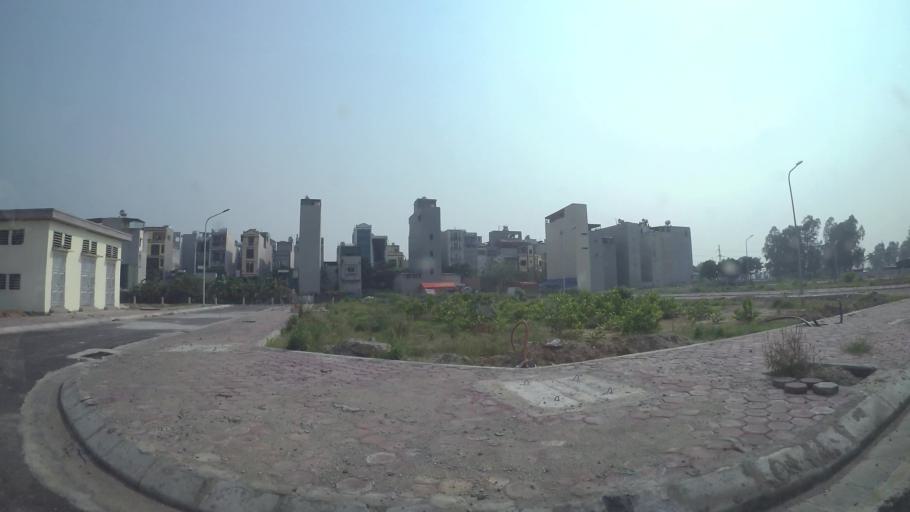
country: VN
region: Ha Noi
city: Ha Dong
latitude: 20.9517
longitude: 105.7895
